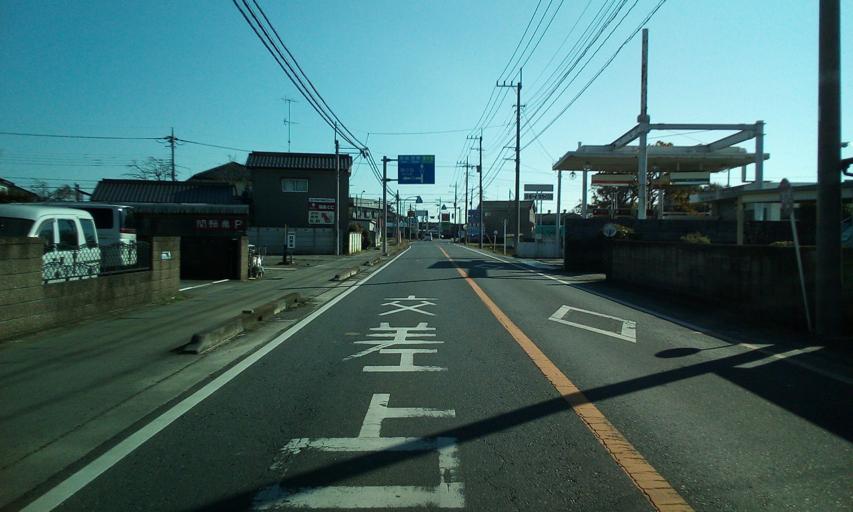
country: JP
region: Ibaraki
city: Sakai
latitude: 36.1298
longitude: 139.7745
